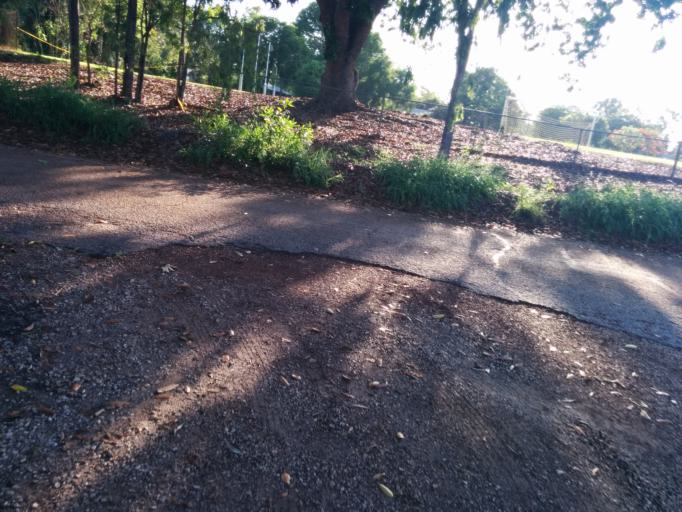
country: AU
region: Northern Territory
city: Alyangula
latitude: -13.8486
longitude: 136.4195
